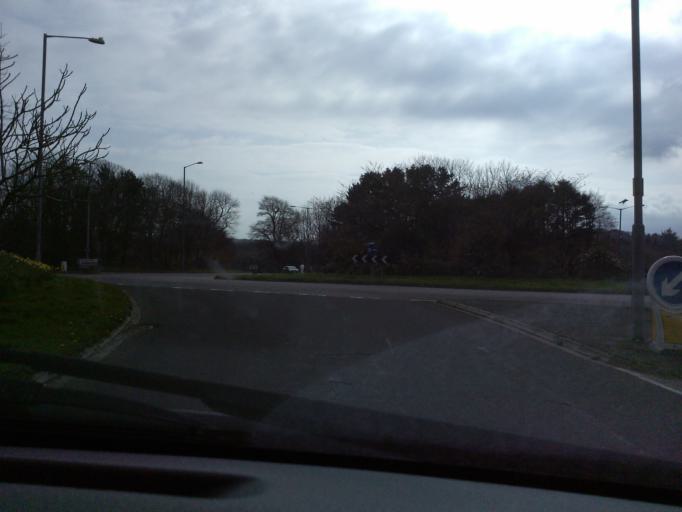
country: GB
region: England
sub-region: Cornwall
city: Penzance
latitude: 50.1259
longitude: -5.5489
